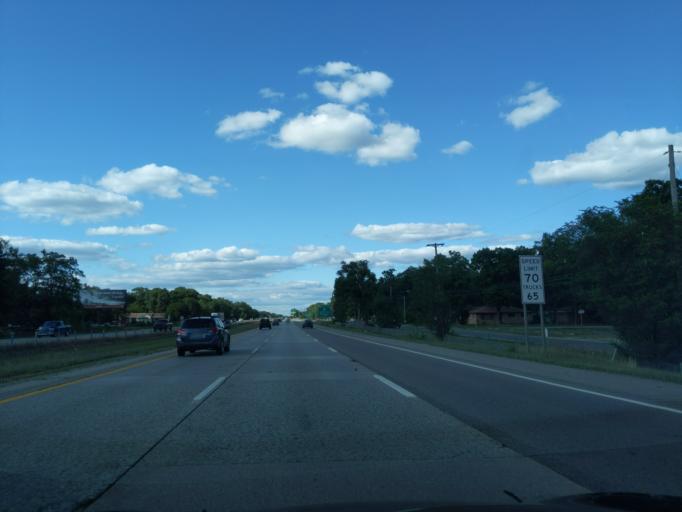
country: US
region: Michigan
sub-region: Muskegon County
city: Muskegon Heights
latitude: 43.2232
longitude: -86.2048
